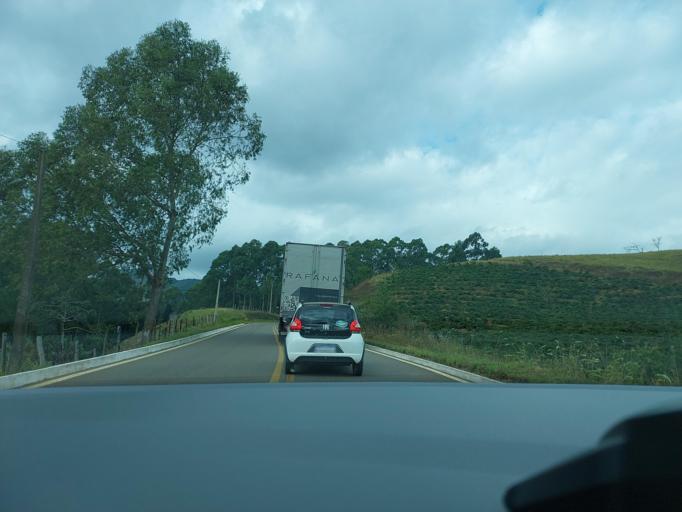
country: BR
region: Minas Gerais
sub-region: Visconde Do Rio Branco
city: Visconde do Rio Branco
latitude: -20.9505
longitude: -42.6125
